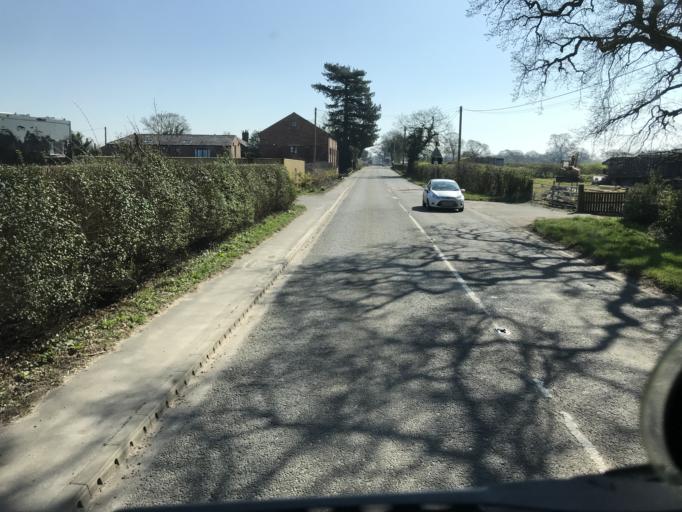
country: GB
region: England
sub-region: Cheshire East
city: Mobberley
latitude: 53.2775
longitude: -2.3014
